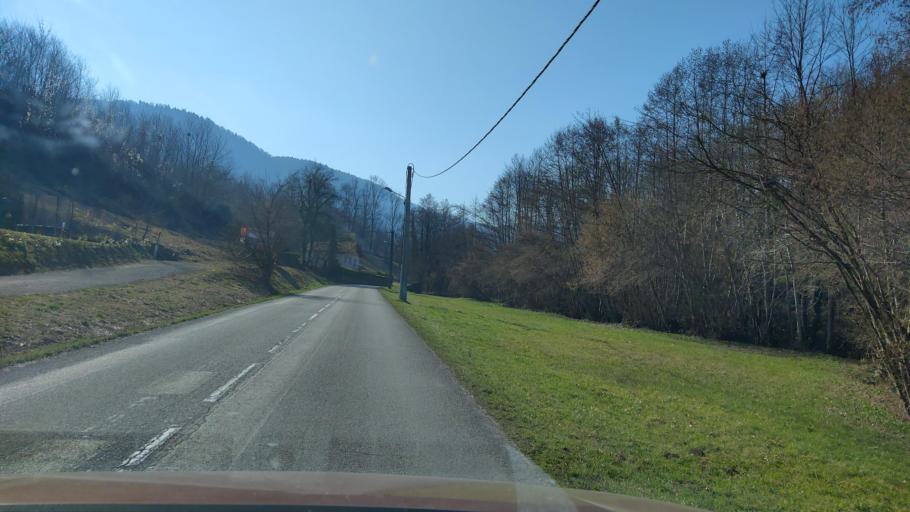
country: FR
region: Rhone-Alpes
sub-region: Departement de la Savoie
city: La Bridoire
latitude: 45.5222
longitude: 5.7393
